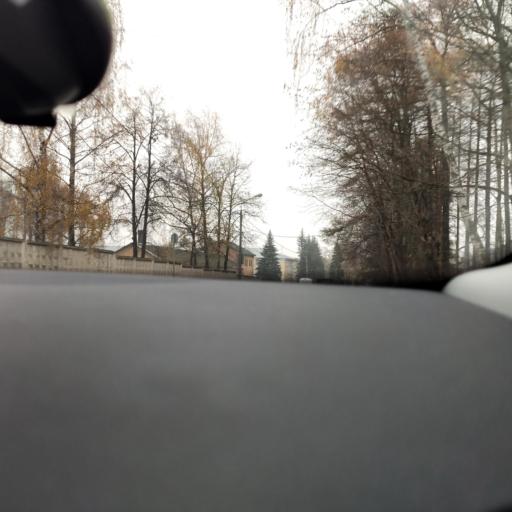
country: RU
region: Moskovskaya
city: Nakhabino
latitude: 55.8418
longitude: 37.1590
